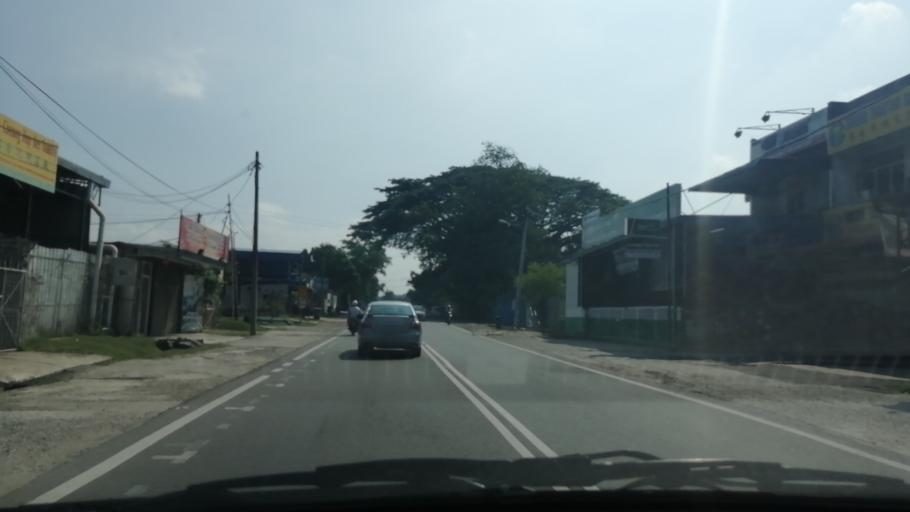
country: MY
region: Kedah
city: Sungai Petani
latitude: 5.6416
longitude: 100.4946
